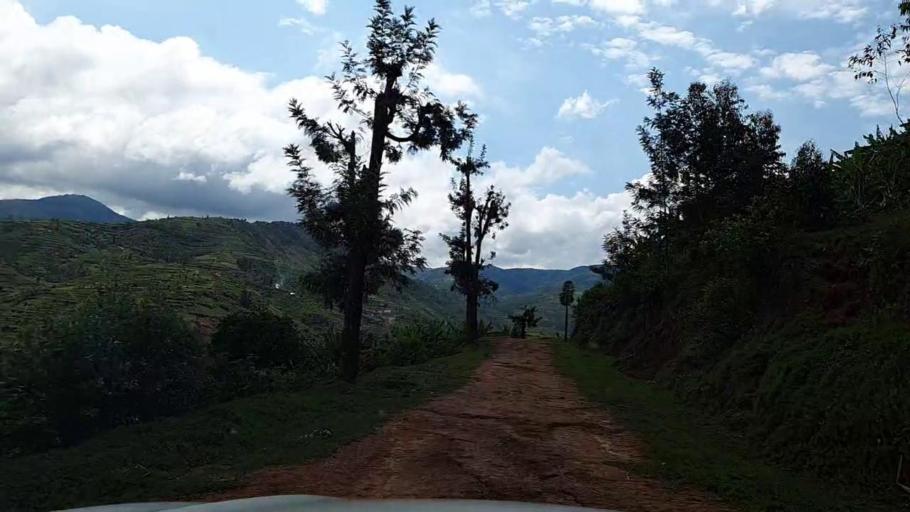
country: RW
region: Southern Province
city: Gikongoro
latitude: -2.3604
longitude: 29.5463
